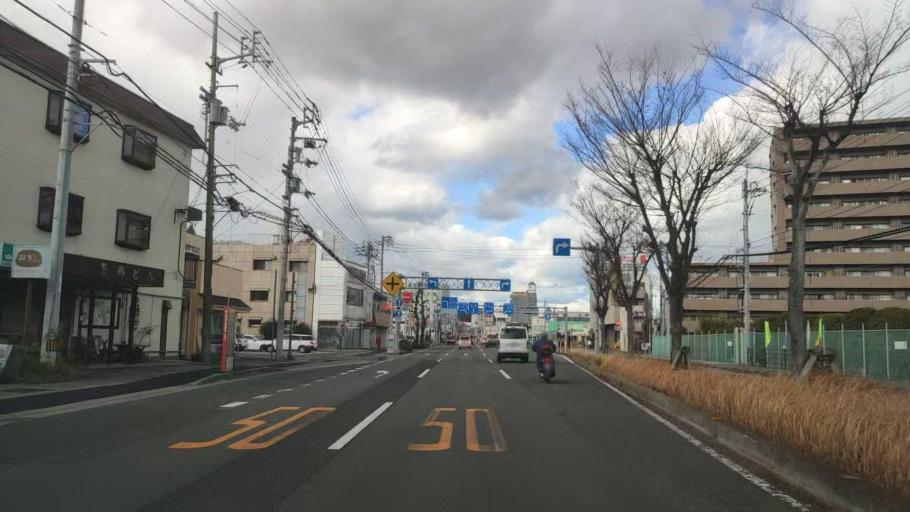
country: JP
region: Ehime
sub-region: Shikoku-chuo Shi
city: Matsuyama
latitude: 33.8210
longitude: 132.7762
